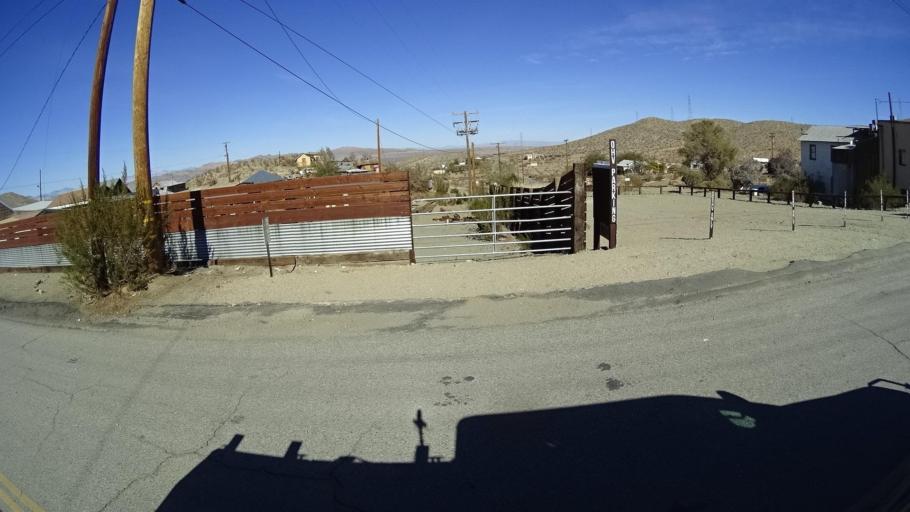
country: US
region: California
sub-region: Kern County
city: Ridgecrest
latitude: 35.3680
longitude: -117.6567
